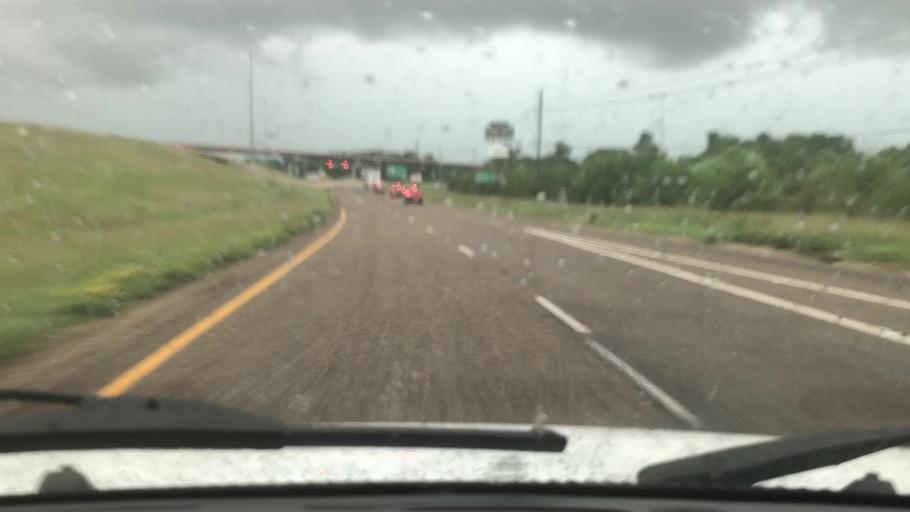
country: US
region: Texas
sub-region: Bowie County
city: Wake Village
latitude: 33.3969
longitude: -94.0986
